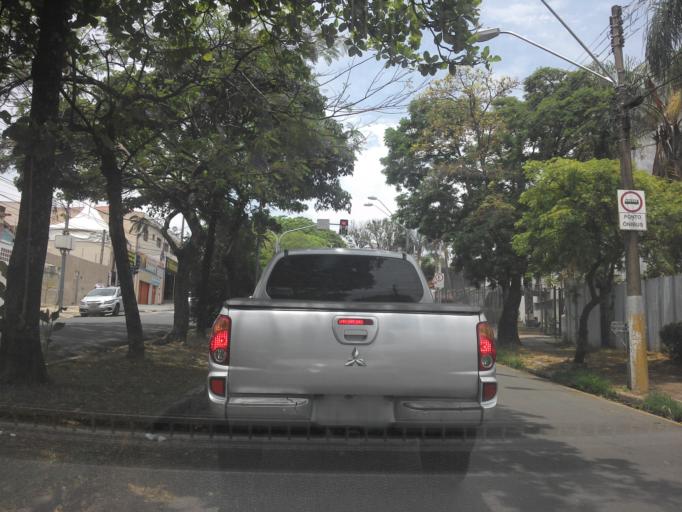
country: BR
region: Sao Paulo
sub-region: Campinas
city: Campinas
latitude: -22.9233
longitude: -47.0416
